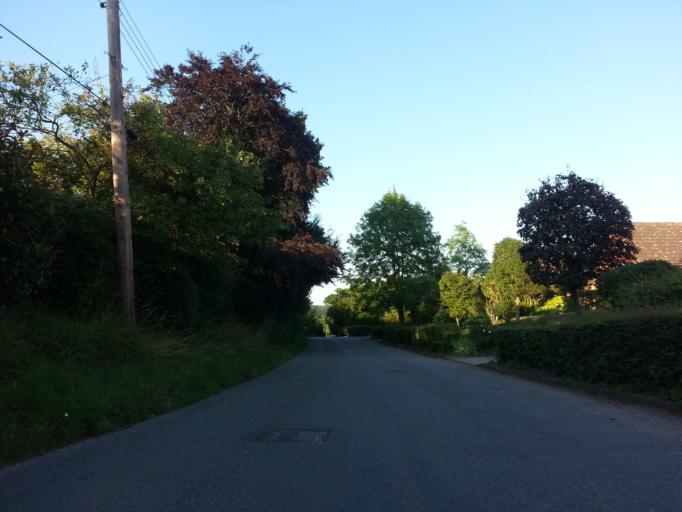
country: GB
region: England
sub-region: Suffolk
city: Ipswich
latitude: 52.0899
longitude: 1.1932
